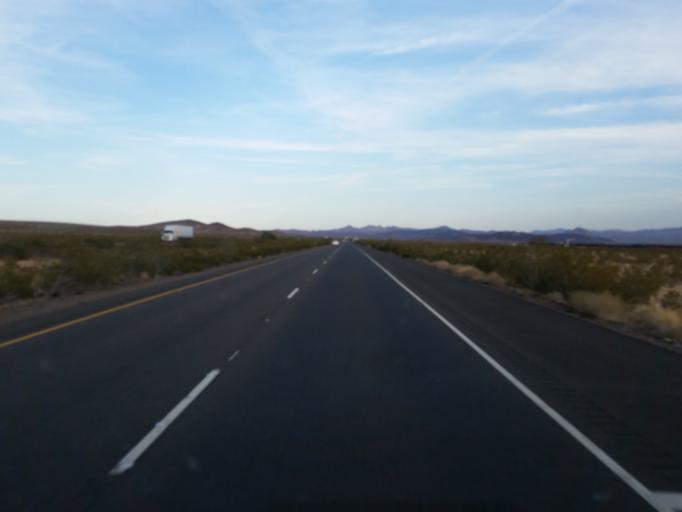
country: US
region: California
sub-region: San Bernardino County
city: Fort Irwin
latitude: 34.7626
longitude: -116.3525
